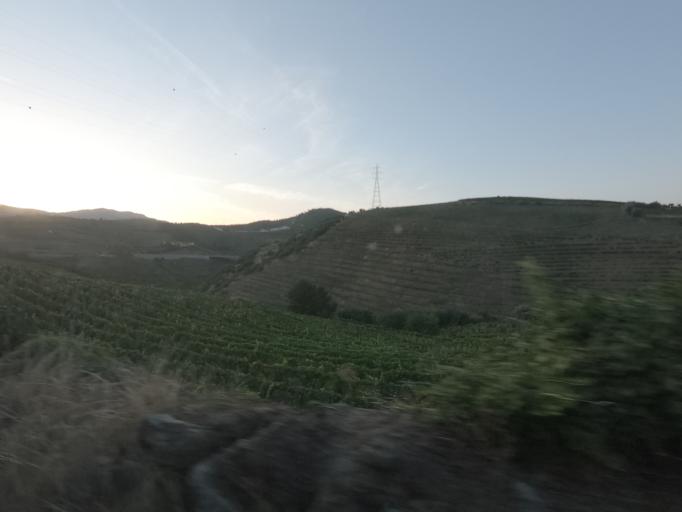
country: PT
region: Vila Real
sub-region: Peso da Regua
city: Peso da Regua
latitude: 41.1651
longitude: -7.7616
